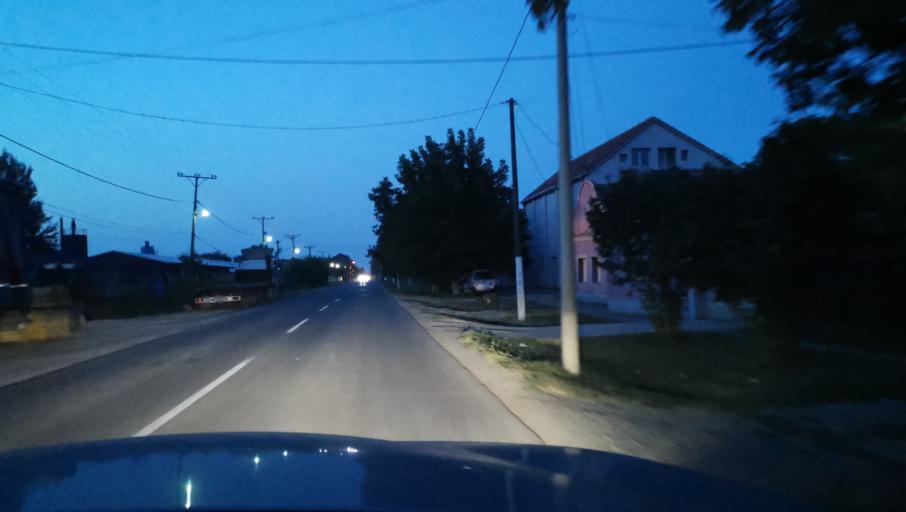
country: RS
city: Boljevci
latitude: 44.7255
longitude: 20.2393
